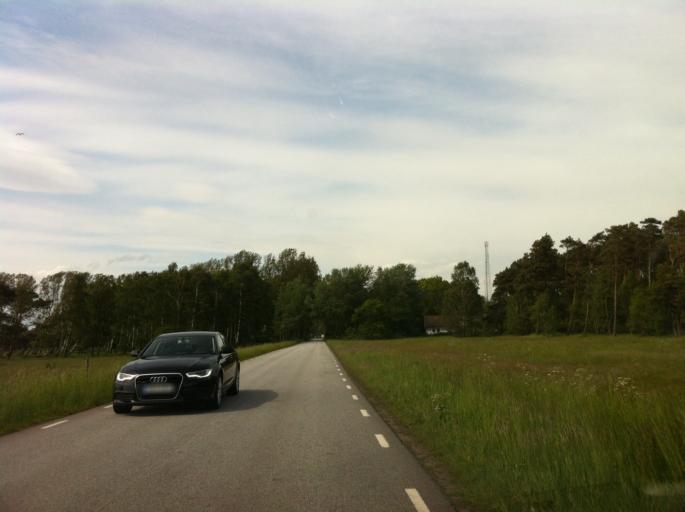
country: SE
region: Skane
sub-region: Kavlinge Kommun
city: Hofterup
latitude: 55.8167
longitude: 12.9335
